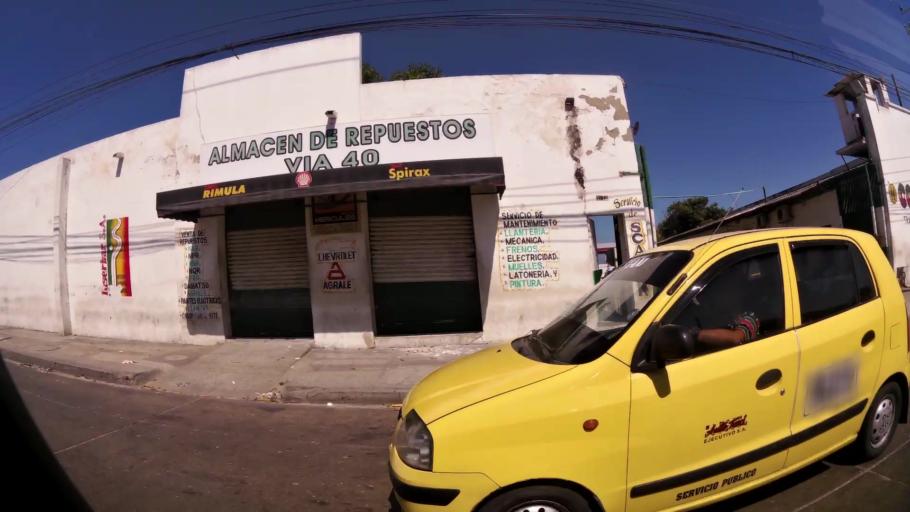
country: CO
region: Atlantico
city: Barranquilla
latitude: 10.9935
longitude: -74.7805
